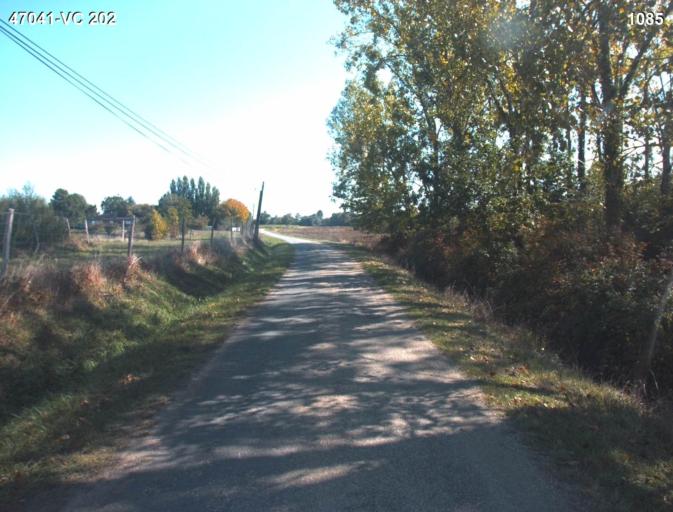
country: FR
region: Aquitaine
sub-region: Departement du Lot-et-Garonne
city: Port-Sainte-Marie
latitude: 44.2155
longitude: 0.4057
